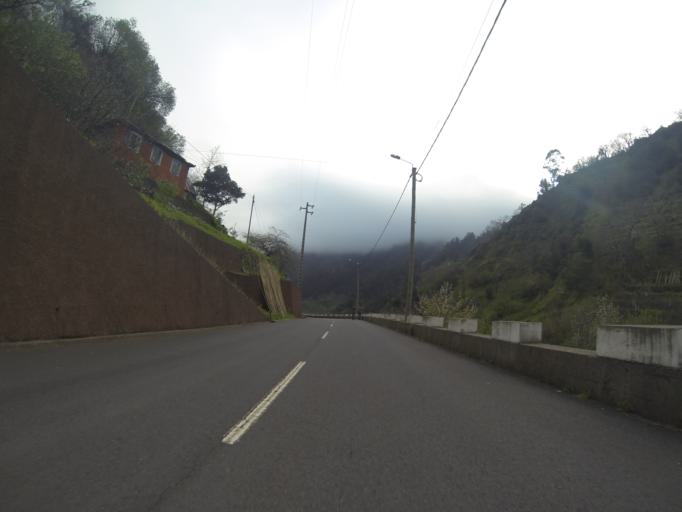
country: PT
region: Madeira
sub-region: Camara de Lobos
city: Curral das Freiras
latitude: 32.7400
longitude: -16.9685
